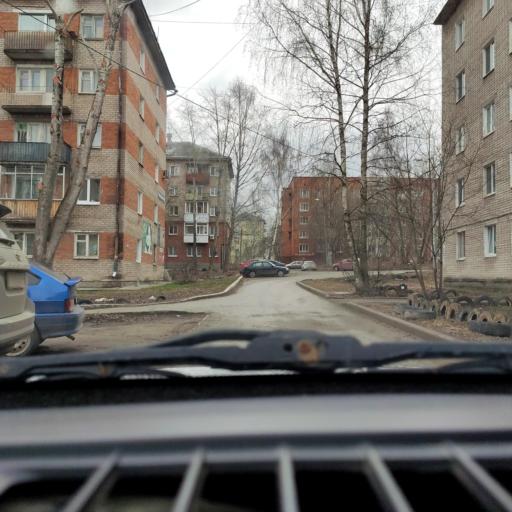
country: RU
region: Perm
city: Perm
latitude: 58.1151
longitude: 56.3157
